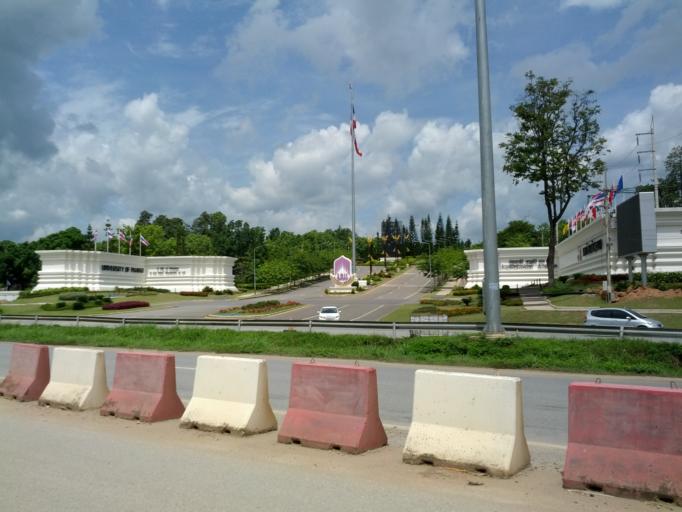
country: TH
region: Phayao
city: Dok Kham Tai
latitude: 19.0310
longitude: 99.9268
